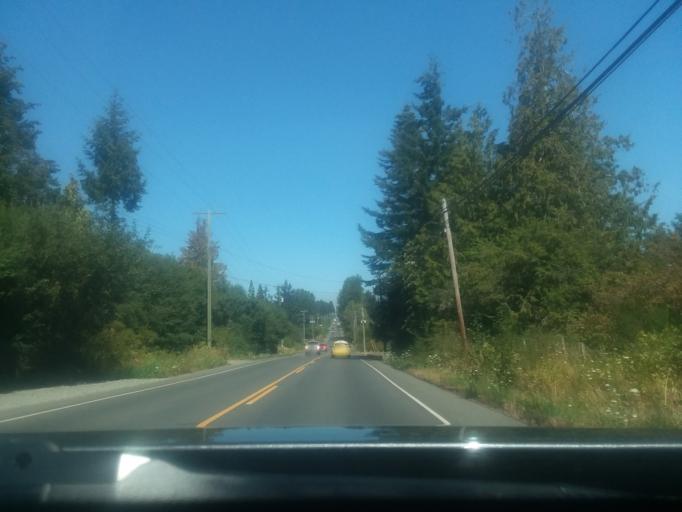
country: CA
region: British Columbia
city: Courtenay
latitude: 49.6910
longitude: -124.9347
